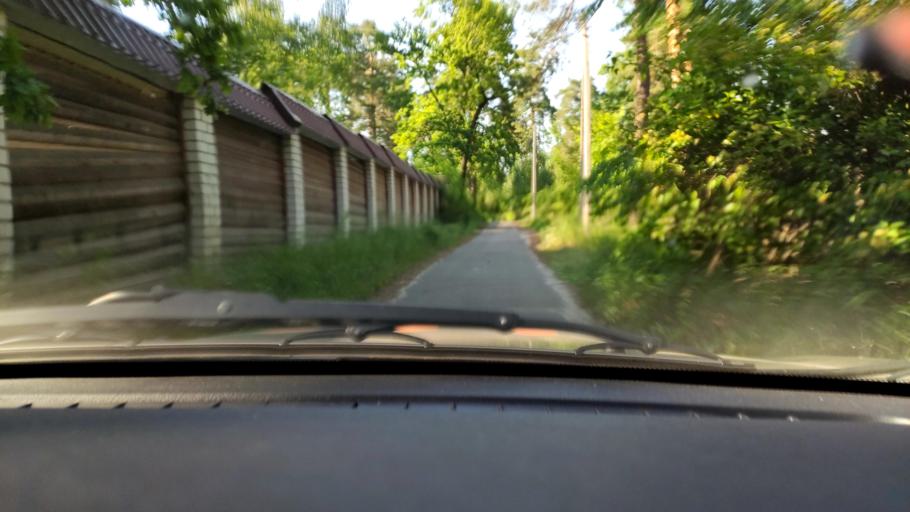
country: RU
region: Voronezj
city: Somovo
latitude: 51.7513
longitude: 39.3744
